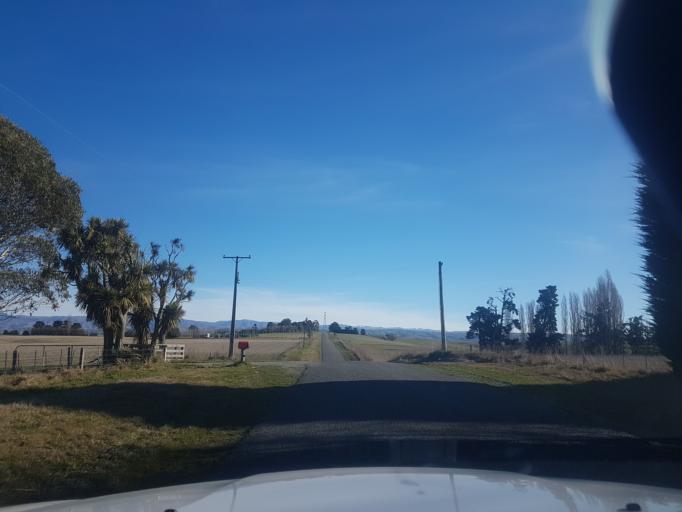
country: NZ
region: Canterbury
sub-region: Timaru District
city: Pleasant Point
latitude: -44.2523
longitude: 171.0504
